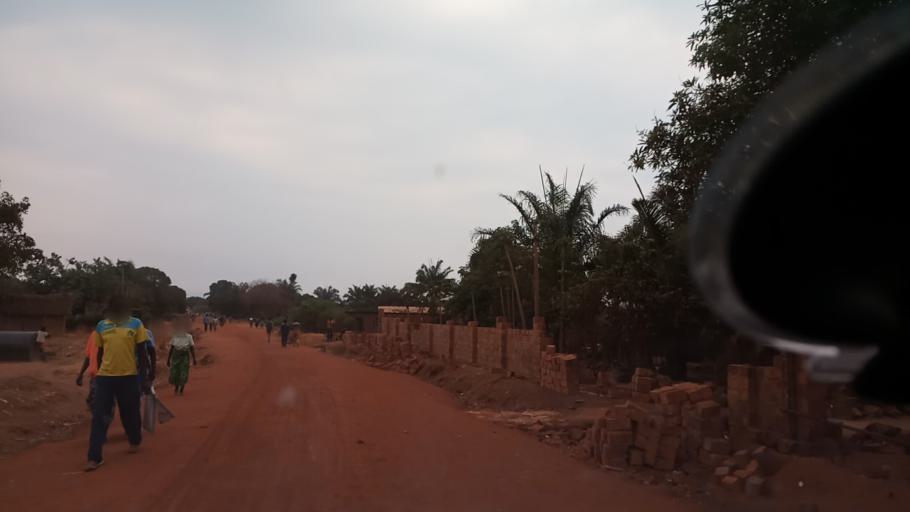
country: ZM
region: Luapula
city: Nchelenge
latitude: -9.2768
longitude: 28.3315
